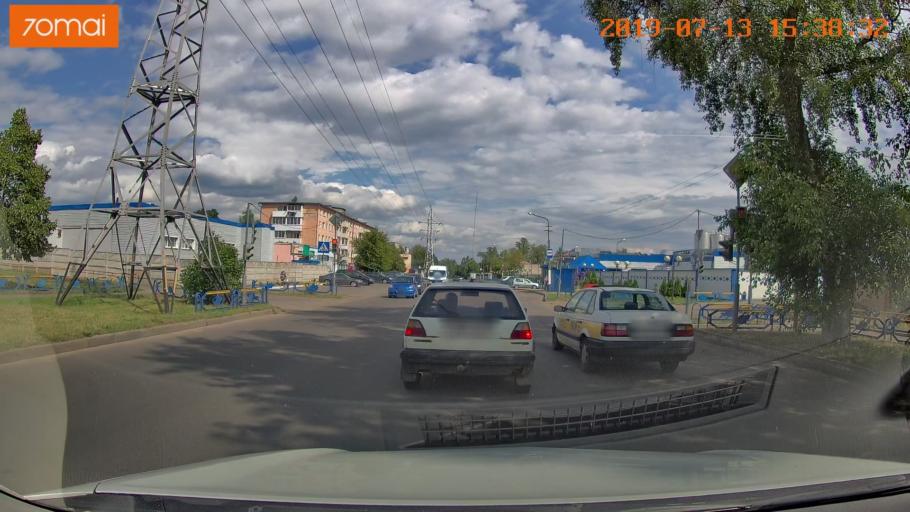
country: BY
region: Mogilev
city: Babruysk
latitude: 53.1362
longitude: 29.1760
